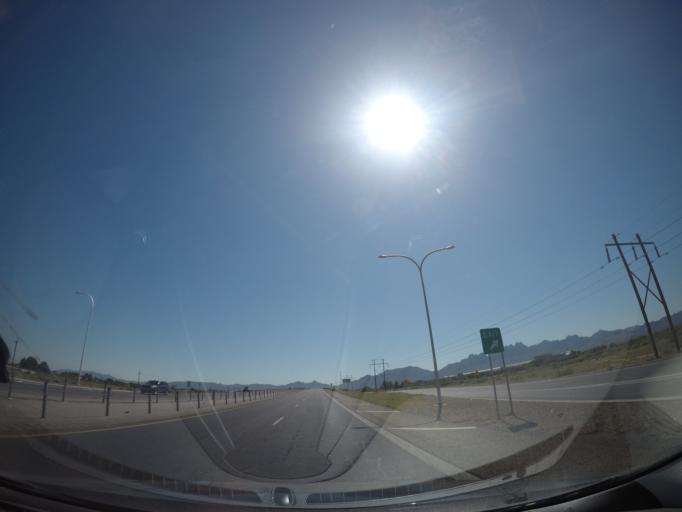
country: US
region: New Mexico
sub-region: Dona Ana County
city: Las Cruces
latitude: 32.3830
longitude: -106.7209
